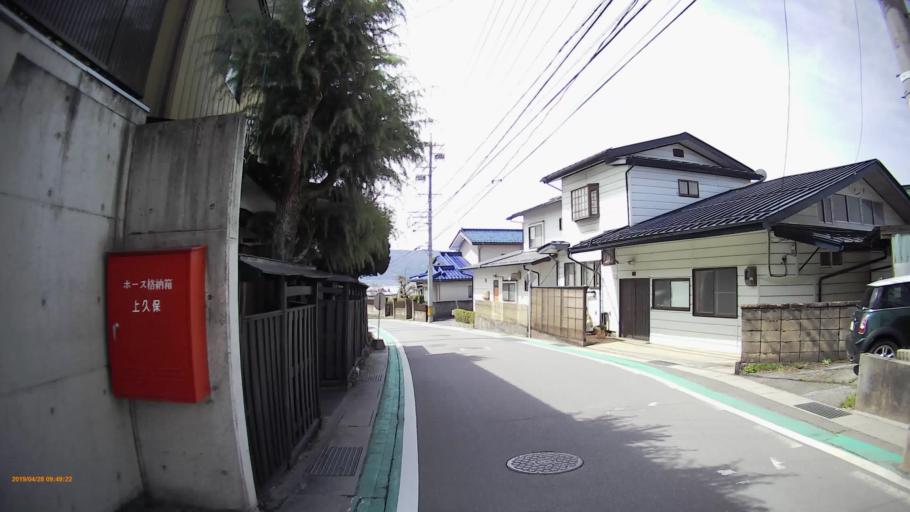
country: JP
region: Nagano
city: Suwa
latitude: 36.0740
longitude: 138.0897
